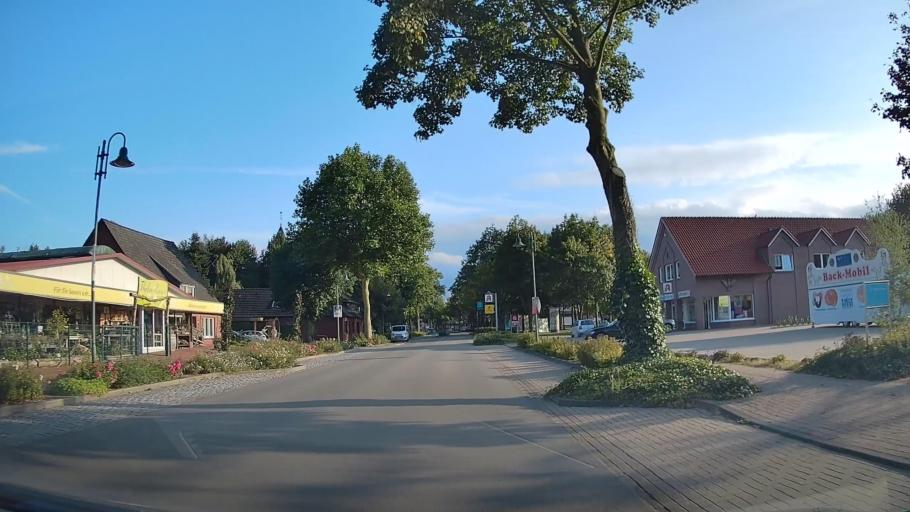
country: DE
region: Lower Saxony
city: Hilkenbrook
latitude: 53.0451
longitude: 7.7373
